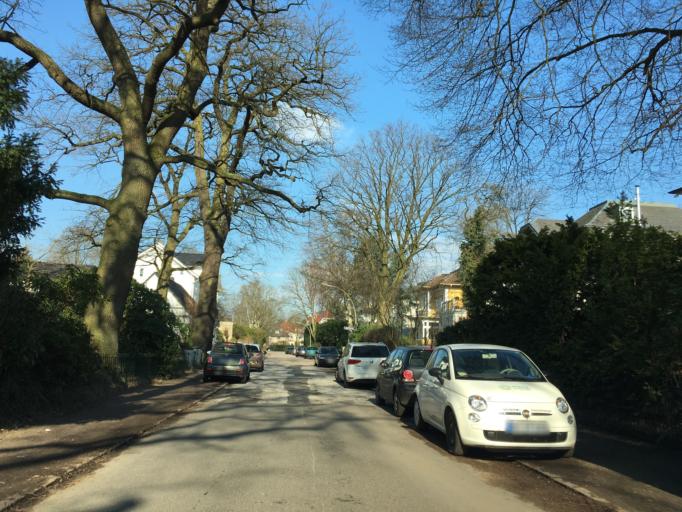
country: DE
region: Hamburg
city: Eidelstedt
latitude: 53.5603
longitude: 9.8782
